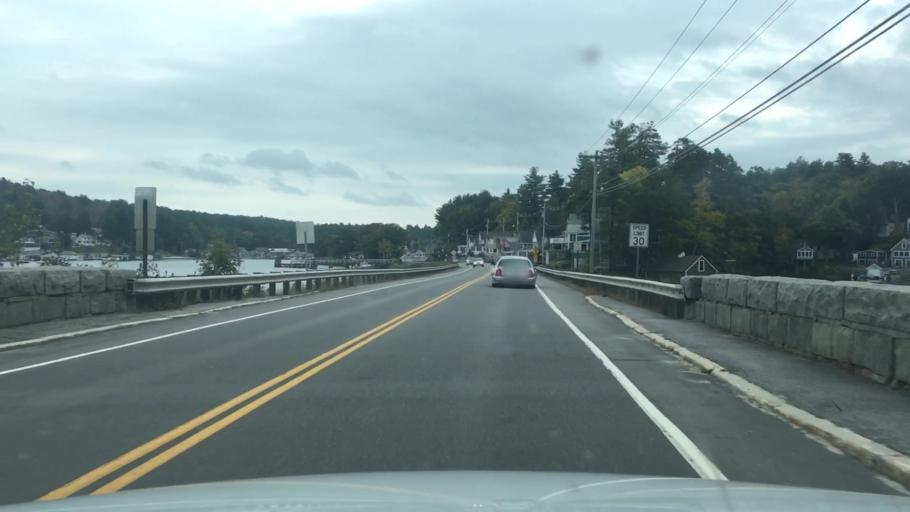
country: US
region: New Hampshire
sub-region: Strafford County
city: New Durham
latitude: 43.4765
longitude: -71.2400
